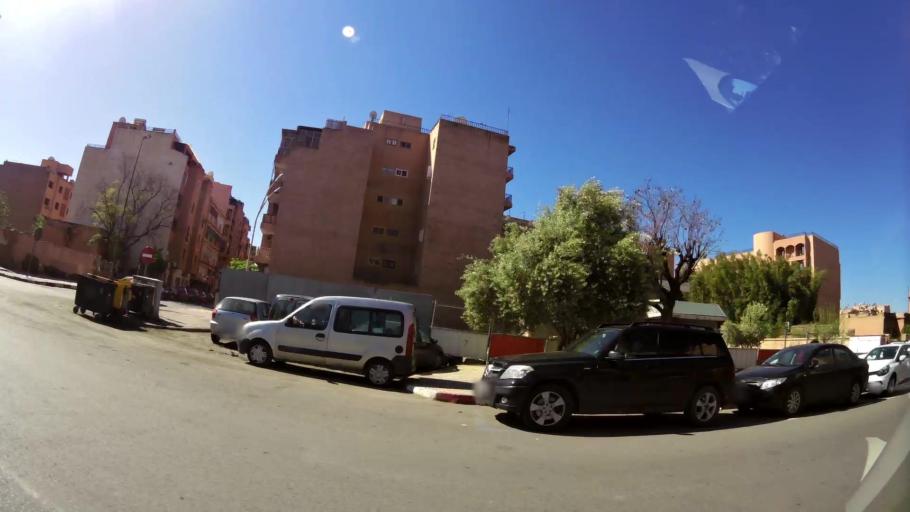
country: MA
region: Marrakech-Tensift-Al Haouz
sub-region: Marrakech
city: Marrakesh
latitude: 31.6325
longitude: -8.0134
